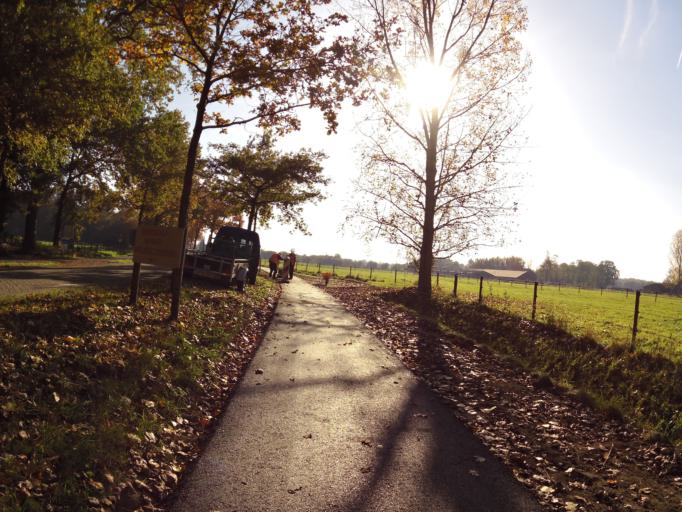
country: NL
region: North Brabant
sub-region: Gemeente Vught
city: Vught
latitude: 51.6330
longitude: 5.2805
